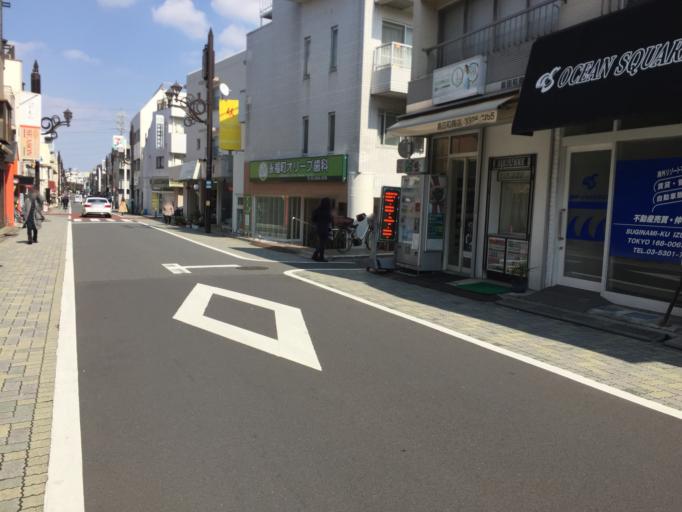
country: JP
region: Tokyo
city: Tokyo
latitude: 35.6779
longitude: 139.6451
